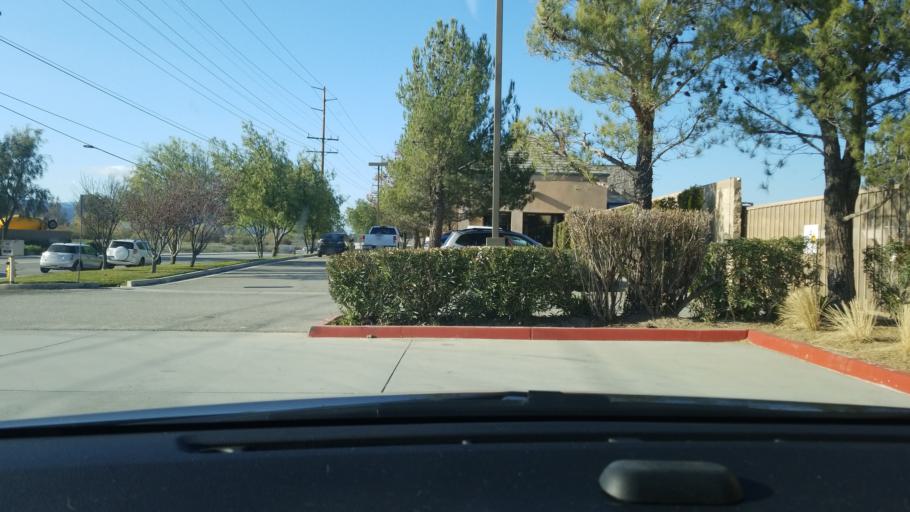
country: US
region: California
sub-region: Riverside County
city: Murrieta
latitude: 33.5330
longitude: -117.1854
